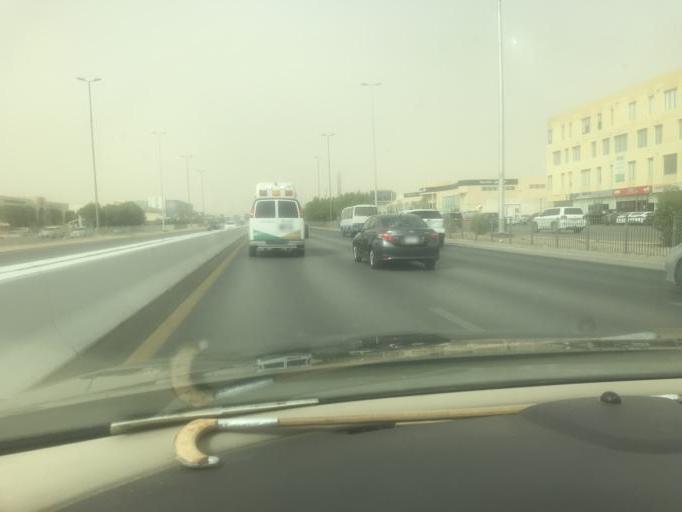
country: SA
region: Ar Riyad
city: Riyadh
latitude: 24.6988
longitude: 46.7376
